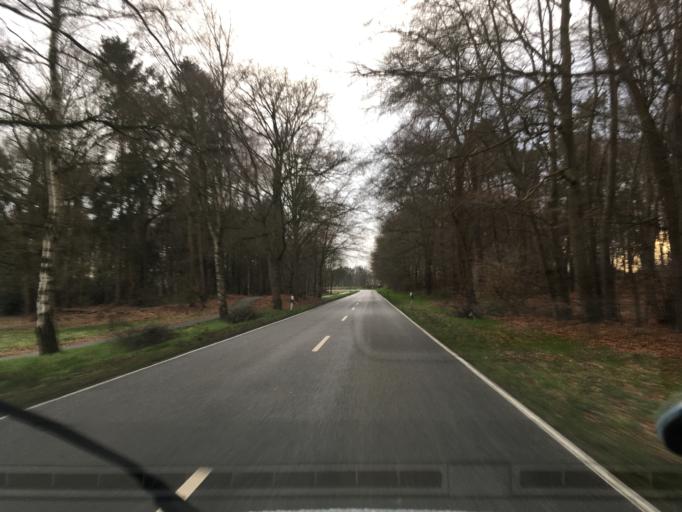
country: DE
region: North Rhine-Westphalia
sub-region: Regierungsbezirk Munster
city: Schoppingen
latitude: 52.0928
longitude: 7.2124
